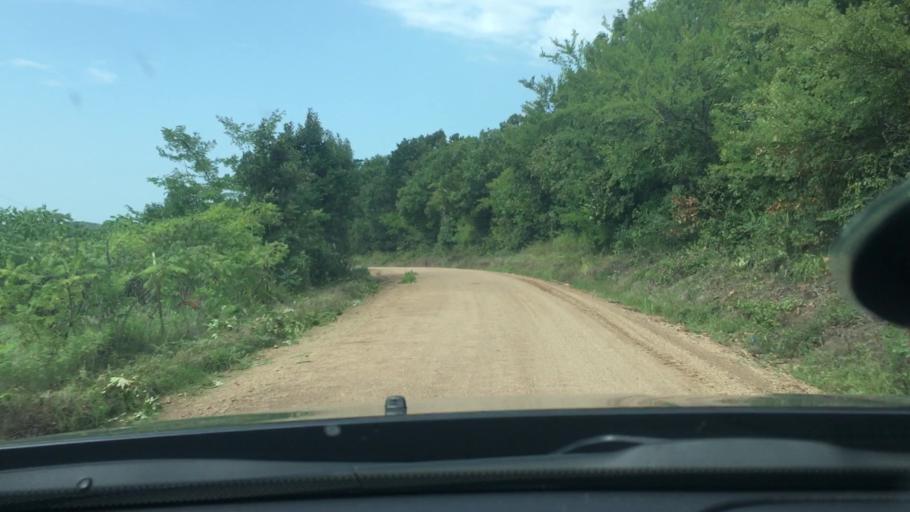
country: US
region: Oklahoma
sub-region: Atoka County
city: Atoka
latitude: 34.4408
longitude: -96.0600
